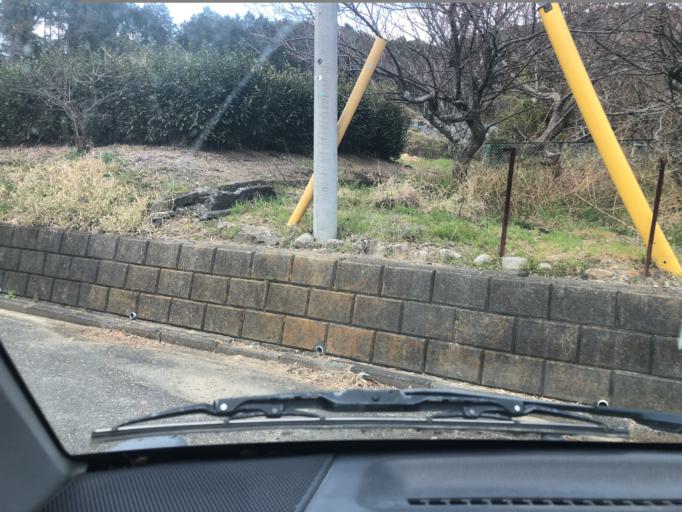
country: JP
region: Shizuoka
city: Mori
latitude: 34.8137
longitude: 137.9493
